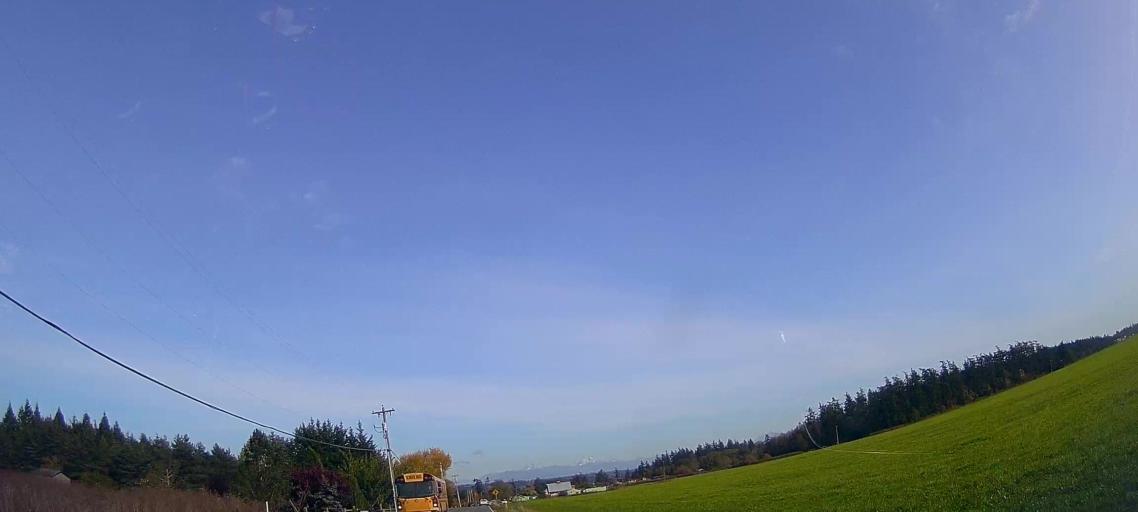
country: US
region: Washington
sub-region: Snohomish County
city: Stanwood
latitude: 48.2544
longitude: -122.4319
